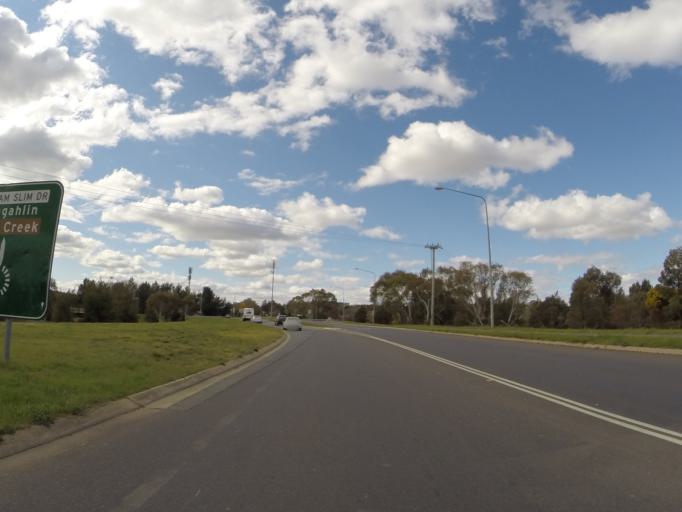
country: AU
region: Australian Capital Territory
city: Belconnen
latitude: -35.2147
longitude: 149.0861
